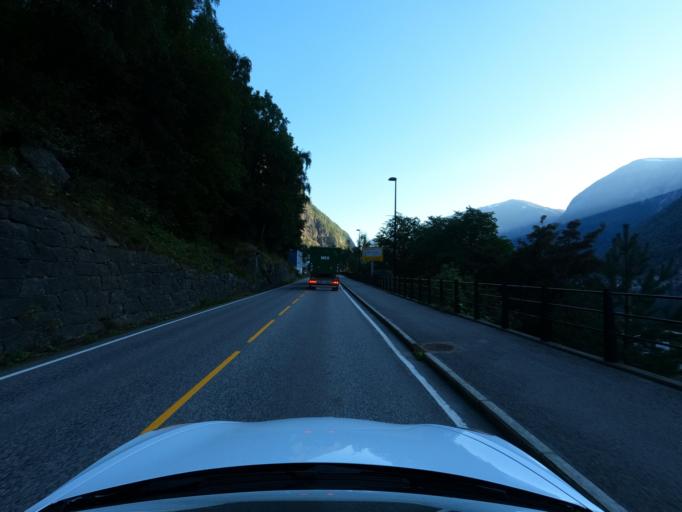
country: NO
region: Hordaland
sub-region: Odda
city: Odda
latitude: 60.1201
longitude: 6.5580
